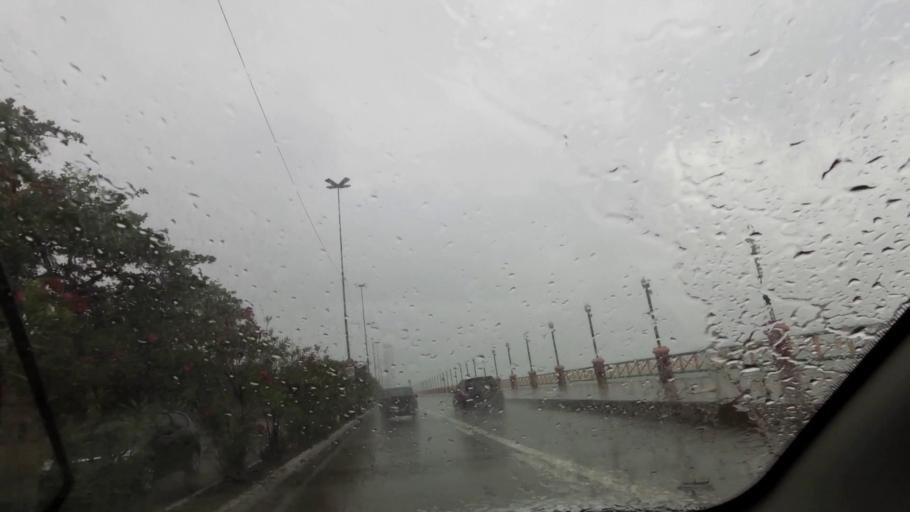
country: BR
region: Pernambuco
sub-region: Recife
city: Recife
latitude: -8.0762
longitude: -34.8885
